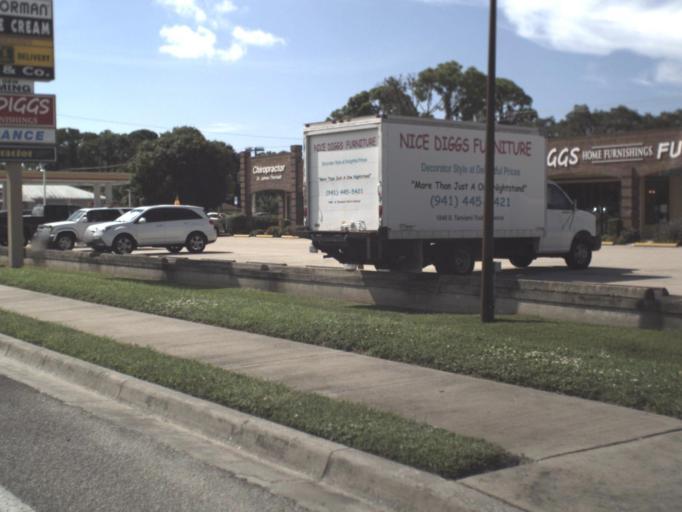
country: US
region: Florida
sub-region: Sarasota County
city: South Venice
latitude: 27.0655
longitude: -82.4190
